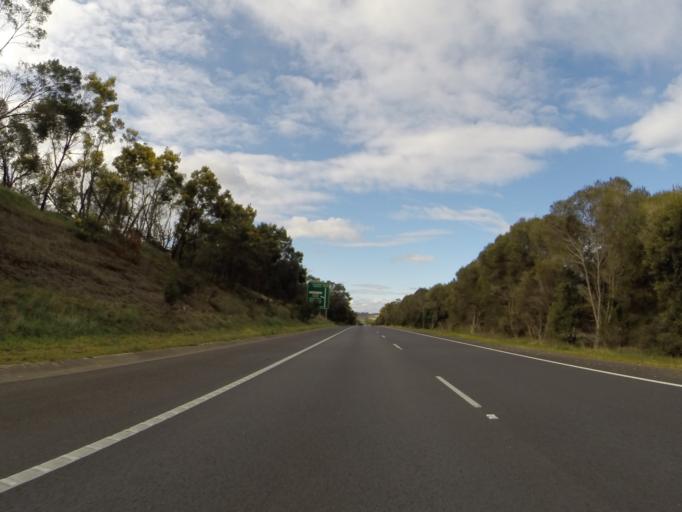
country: AU
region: New South Wales
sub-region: Wingecarribee
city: Bundanoon
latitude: -34.5998
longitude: 150.2367
